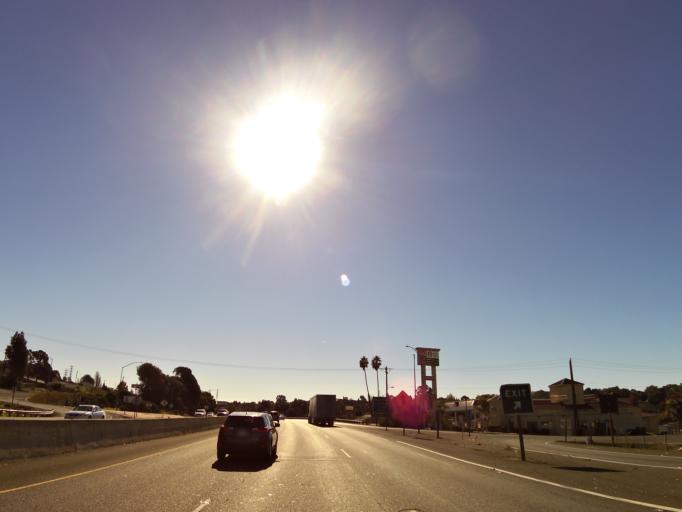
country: US
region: California
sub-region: Solano County
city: Vallejo
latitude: 38.0853
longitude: -122.2331
